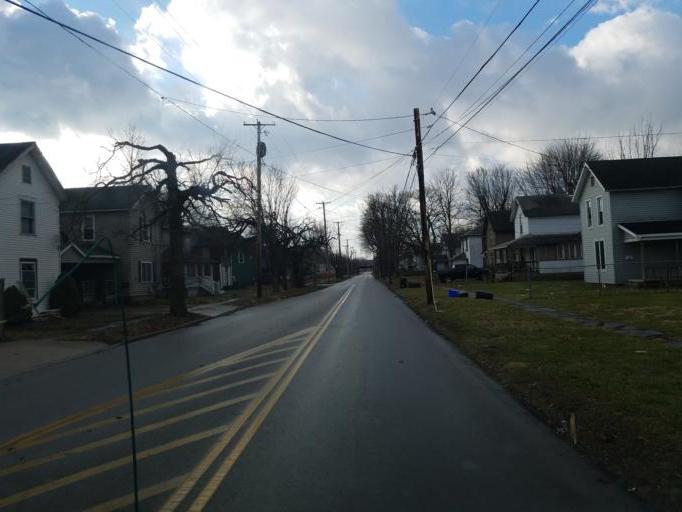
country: US
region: Ohio
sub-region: Marion County
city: Marion
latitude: 40.5927
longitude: -83.1375
